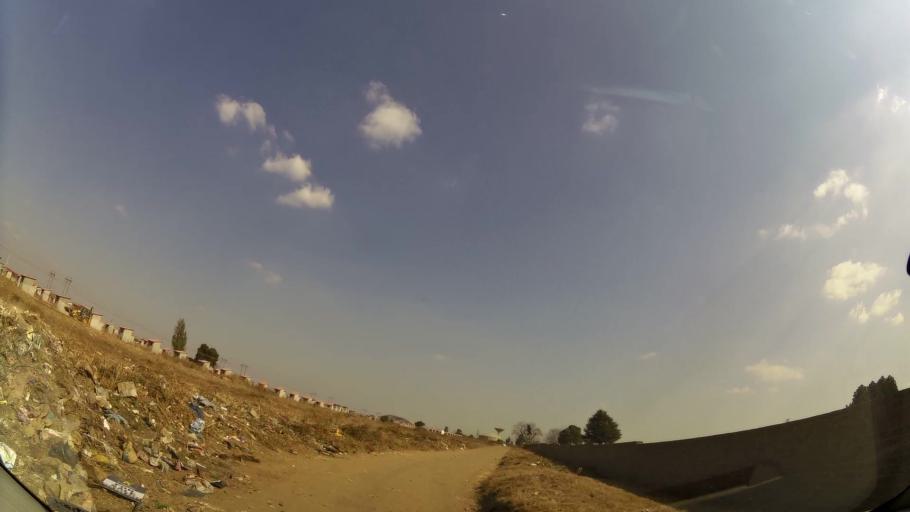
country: ZA
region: Gauteng
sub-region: Ekurhuleni Metropolitan Municipality
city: Benoni
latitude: -26.1394
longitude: 28.4083
